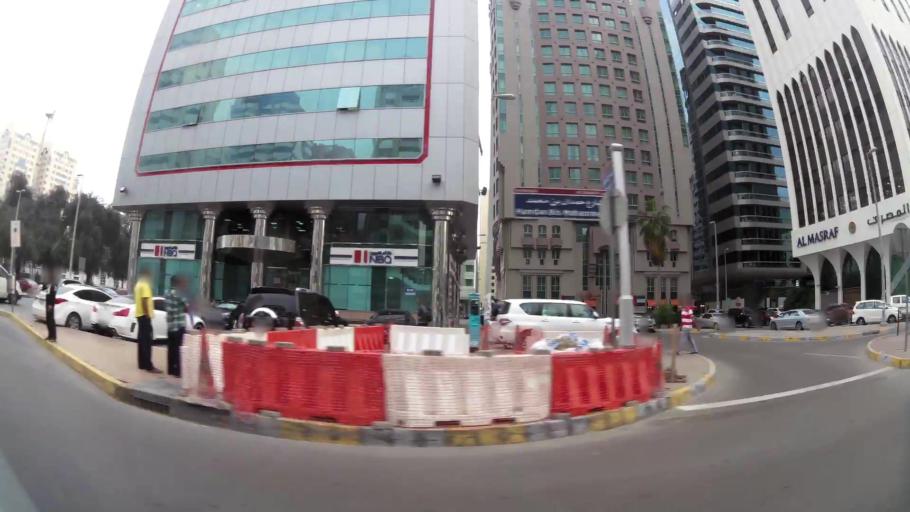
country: AE
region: Abu Dhabi
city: Abu Dhabi
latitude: 24.4979
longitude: 54.3736
